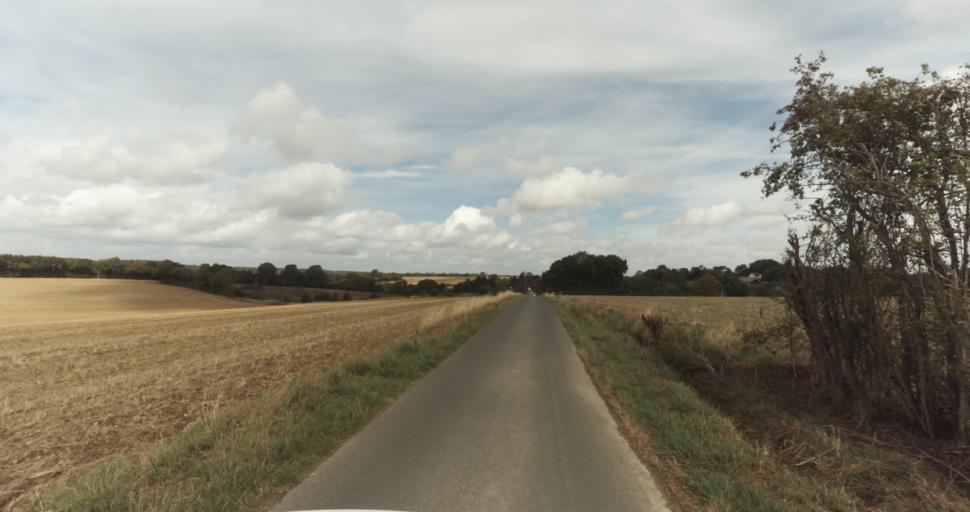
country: FR
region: Lower Normandy
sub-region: Departement de l'Orne
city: Gace
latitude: 48.8071
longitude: 0.3756
